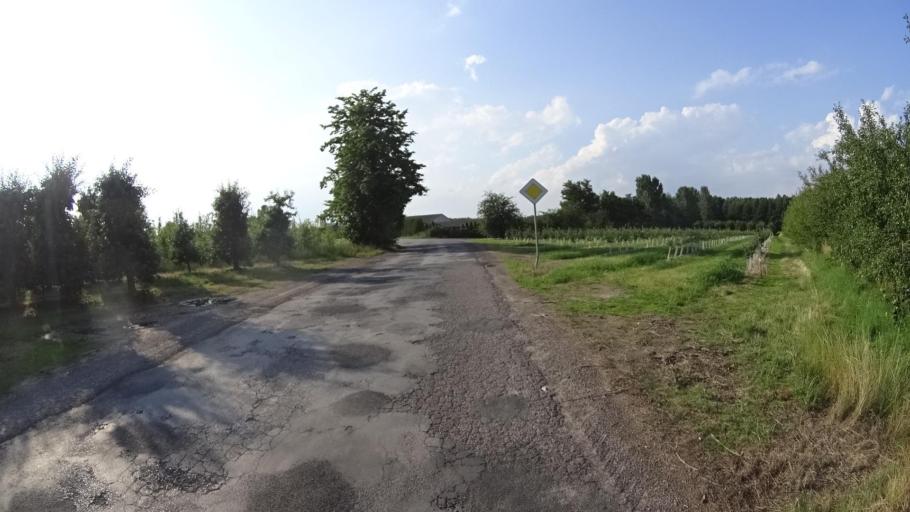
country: PL
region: Masovian Voivodeship
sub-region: Powiat grojecki
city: Goszczyn
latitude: 51.7112
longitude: 20.7909
